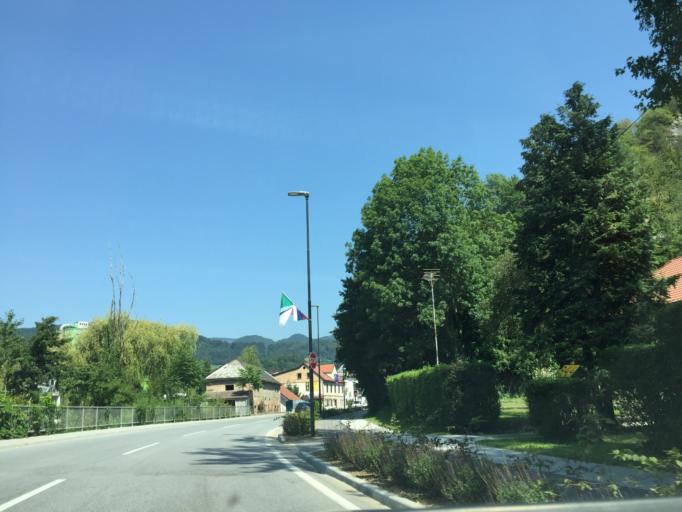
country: SI
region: Zagorje ob Savi
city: Zagorje ob Savi
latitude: 46.1259
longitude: 14.9971
